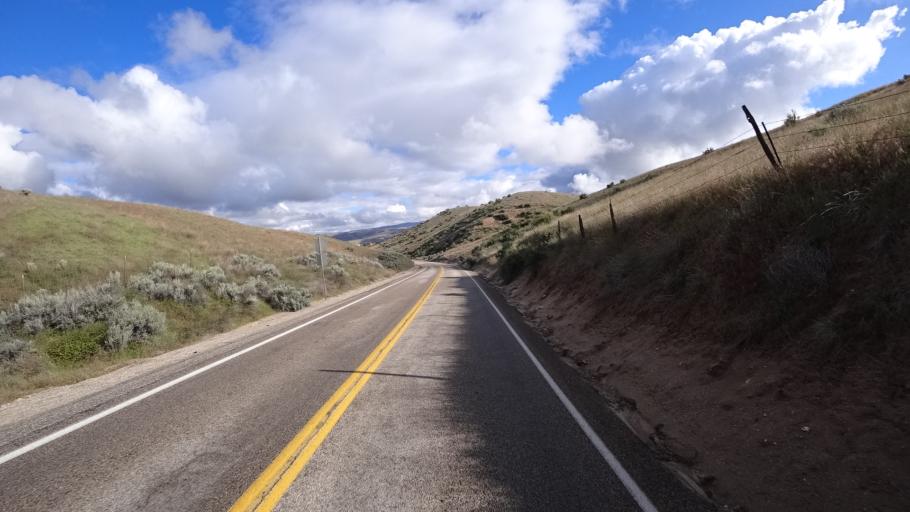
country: US
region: Idaho
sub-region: Ada County
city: Garden City
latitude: 43.7075
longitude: -116.2622
